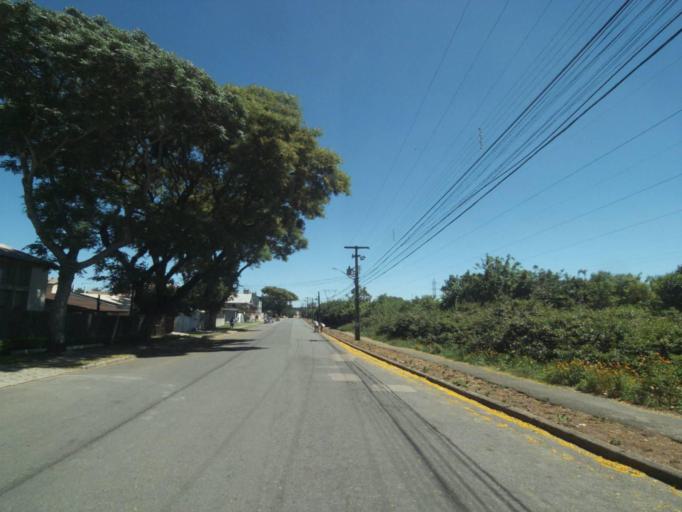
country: BR
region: Parana
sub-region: Curitiba
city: Curitiba
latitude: -25.4750
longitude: -49.3448
